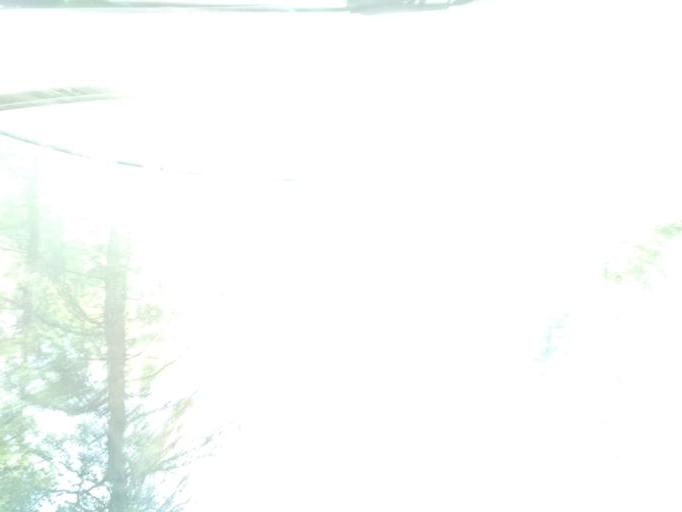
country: GR
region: Central Greece
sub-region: Nomos Evvoias
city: Politika
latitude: 38.6658
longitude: 23.5568
